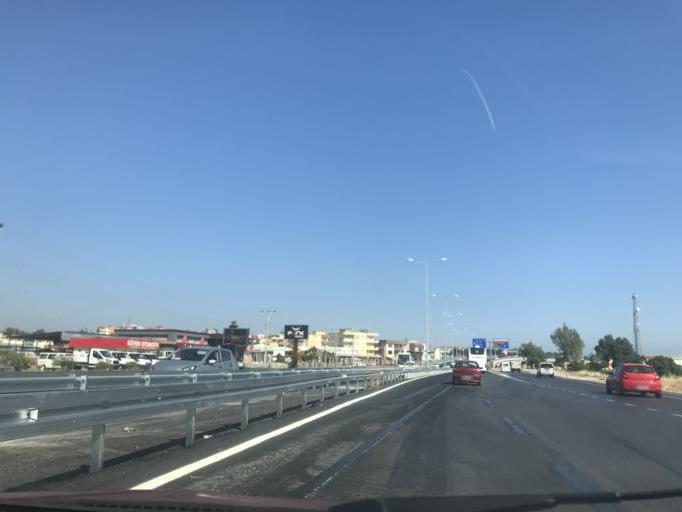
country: TR
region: Antalya
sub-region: Manavgat
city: Side
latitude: 36.7975
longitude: 31.4077
